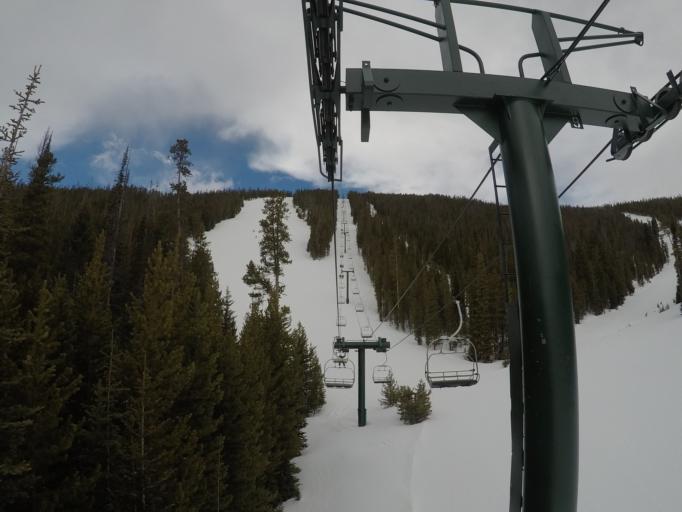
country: US
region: Montana
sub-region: Granite County
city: Philipsburg
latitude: 46.2547
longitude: -113.2431
